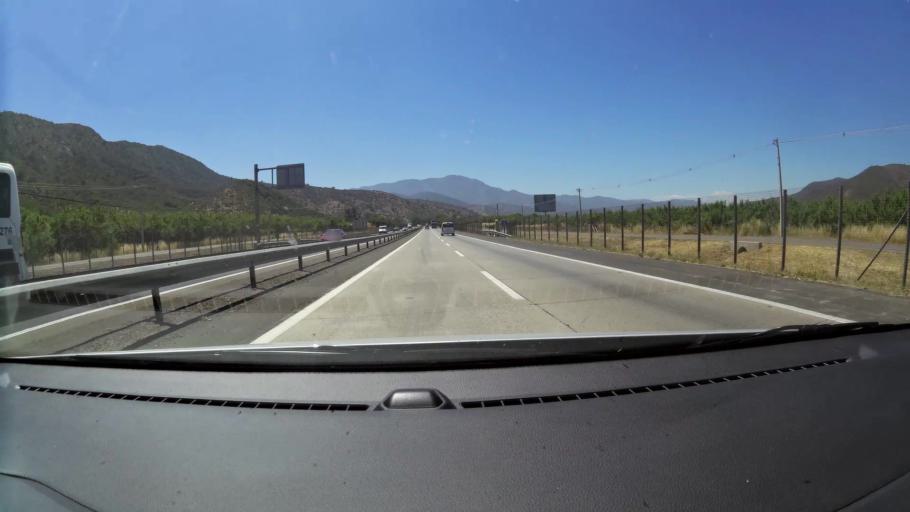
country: CL
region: Santiago Metropolitan
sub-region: Provincia de Chacabuco
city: Lampa
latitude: -33.4011
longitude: -71.1091
